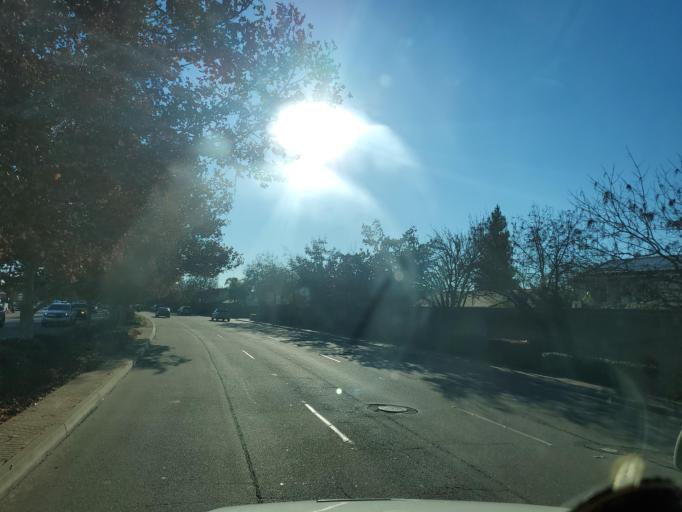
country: US
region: California
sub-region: San Joaquin County
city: August
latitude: 38.0138
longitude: -121.2730
